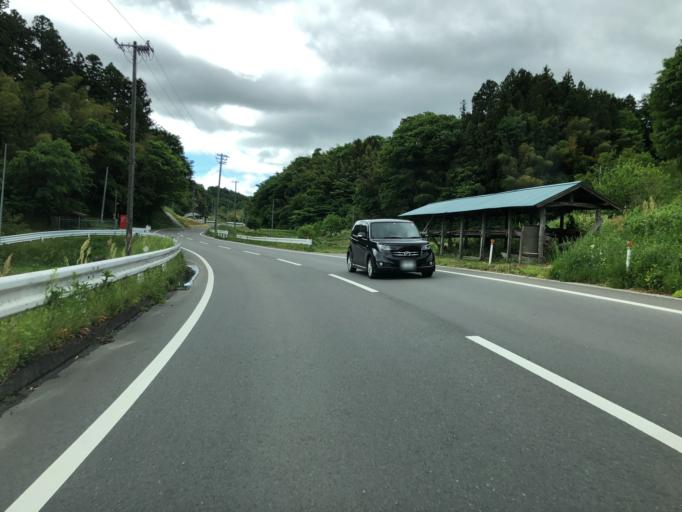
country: JP
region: Fukushima
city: Nihommatsu
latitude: 37.5342
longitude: 140.4572
